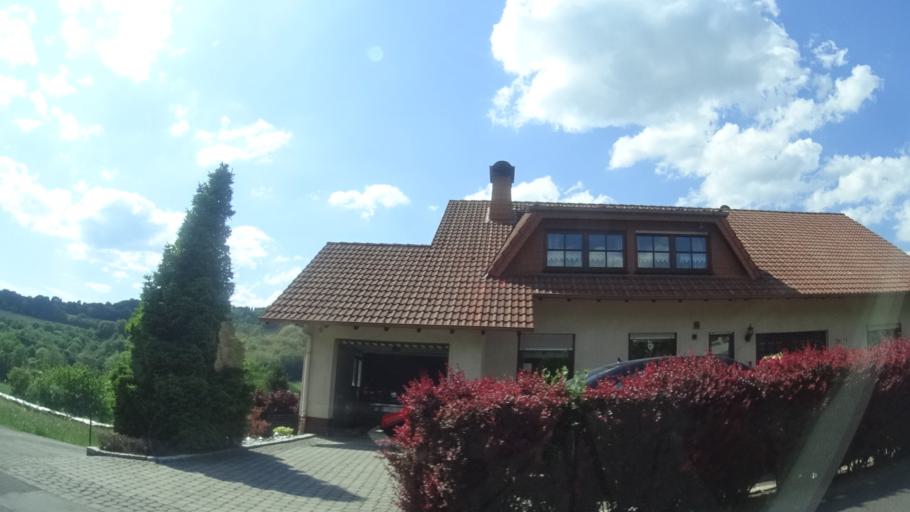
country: DE
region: Hesse
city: Tann
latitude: 50.6348
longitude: 10.0176
